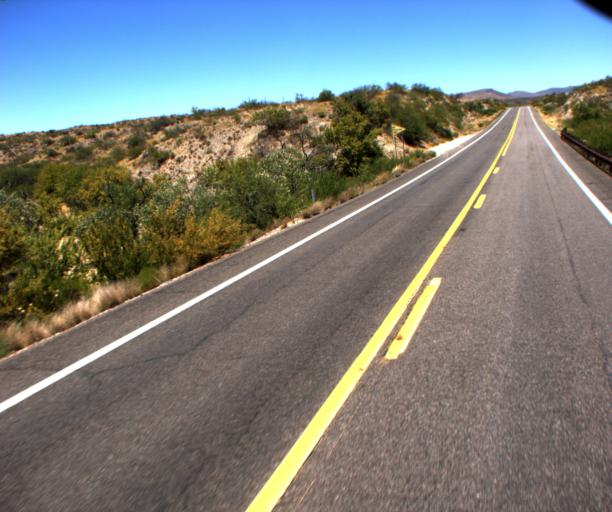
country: US
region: Arizona
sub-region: Gila County
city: Globe
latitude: 33.3532
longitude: -110.7343
